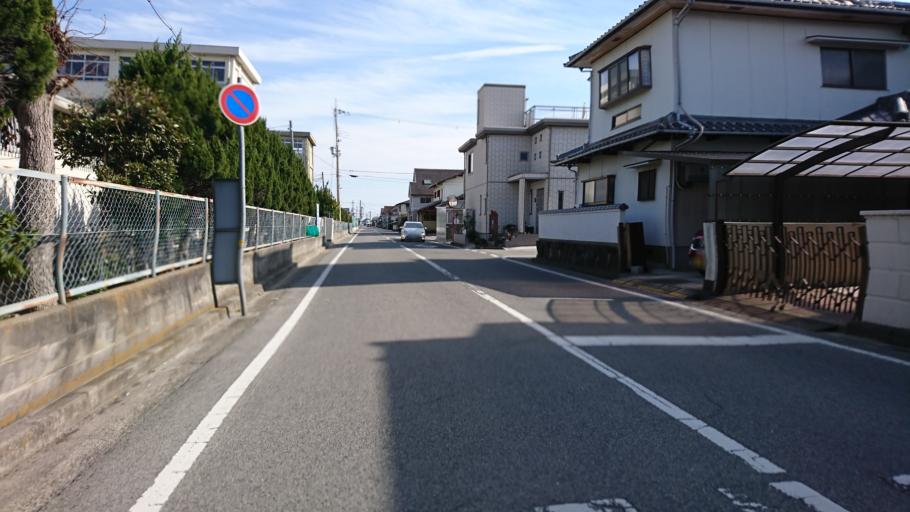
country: JP
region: Hyogo
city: Kakogawacho-honmachi
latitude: 34.7901
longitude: 134.8250
